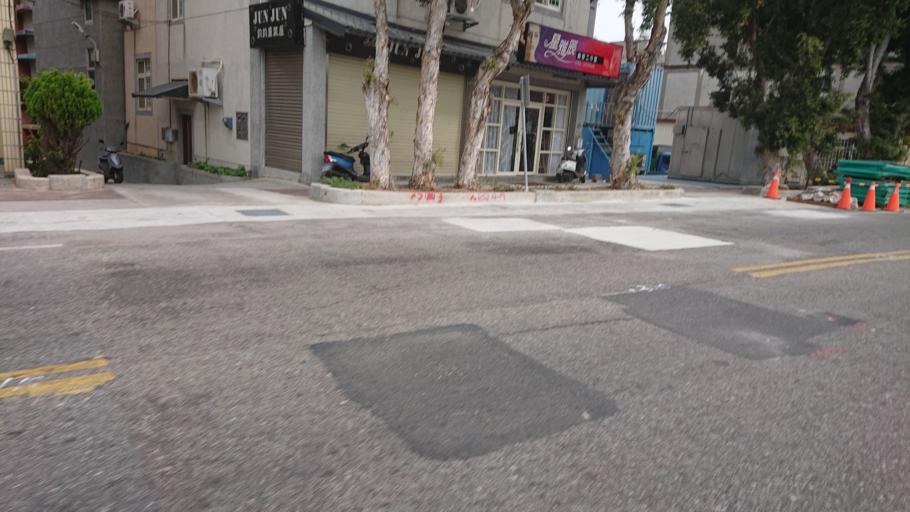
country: TW
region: Fukien
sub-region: Kinmen
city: Jincheng
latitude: 24.4296
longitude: 118.3187
